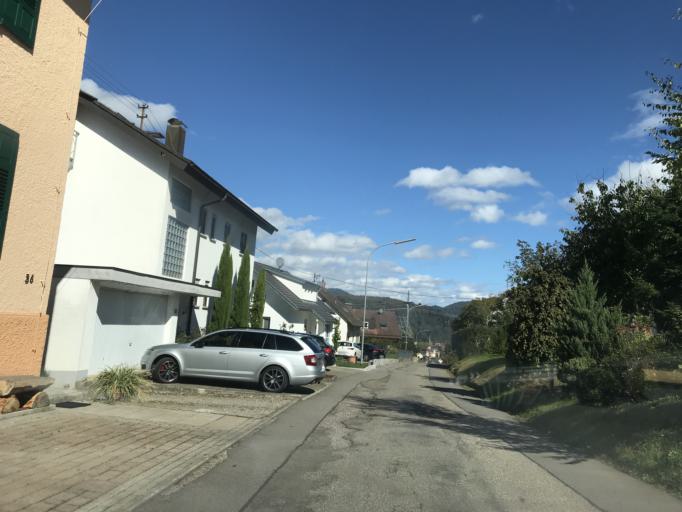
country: DE
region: Baden-Wuerttemberg
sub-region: Freiburg Region
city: Schopfheim
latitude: 47.6385
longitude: 7.8138
